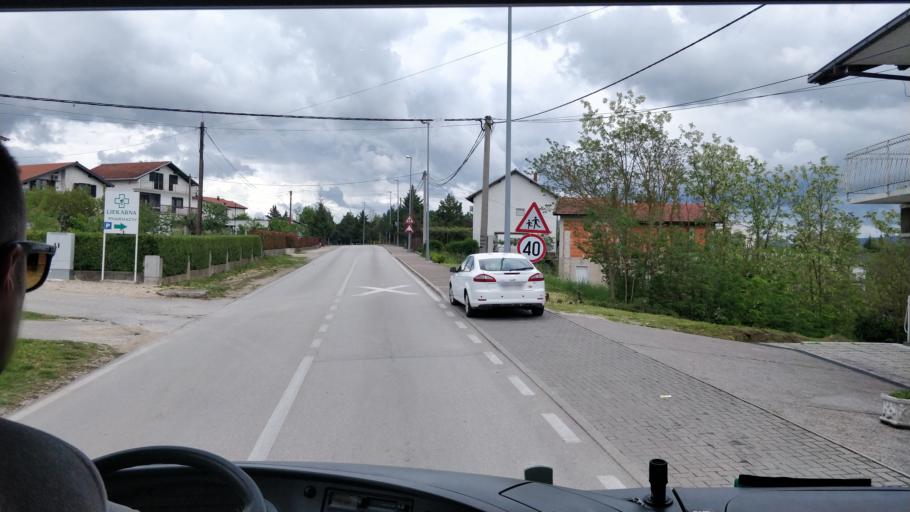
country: BA
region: Federation of Bosnia and Herzegovina
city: Ljubuski
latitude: 43.1835
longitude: 17.5244
